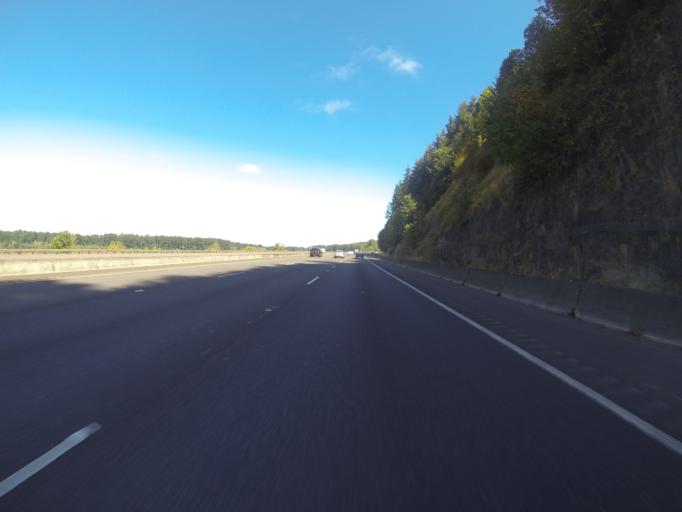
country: US
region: Washington
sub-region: Cowlitz County
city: Kalama
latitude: 46.0670
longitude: -122.8678
